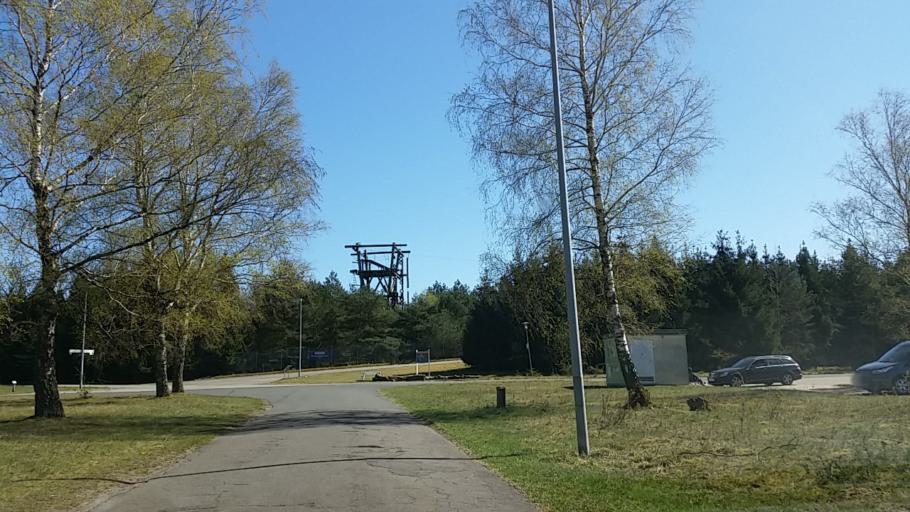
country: DE
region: Lower Saxony
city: Schneverdingen
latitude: 53.1447
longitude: 9.8201
